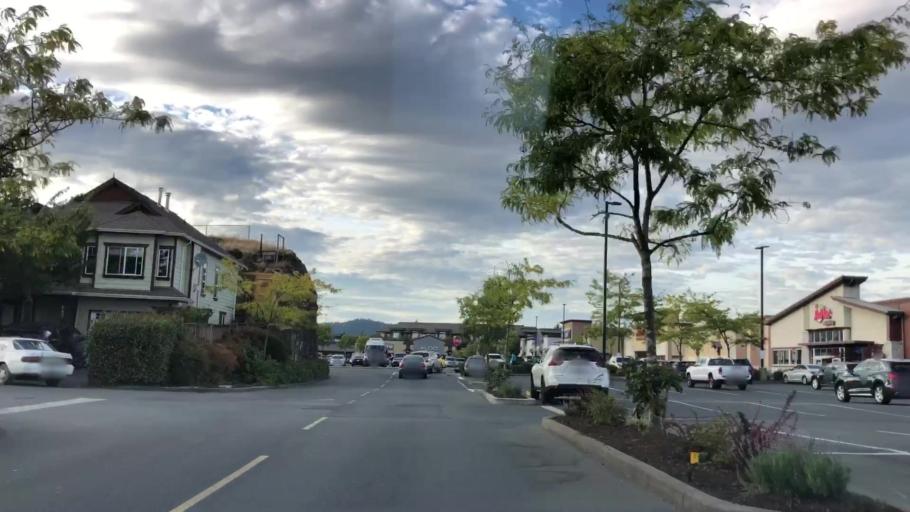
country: CA
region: British Columbia
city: Langford
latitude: 48.4615
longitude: -123.4961
